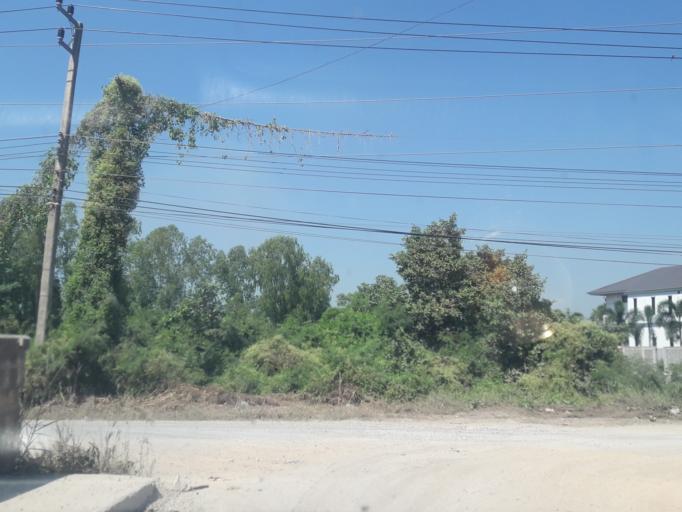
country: TH
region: Sara Buri
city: Nong Khae
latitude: 14.3274
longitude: 100.8710
